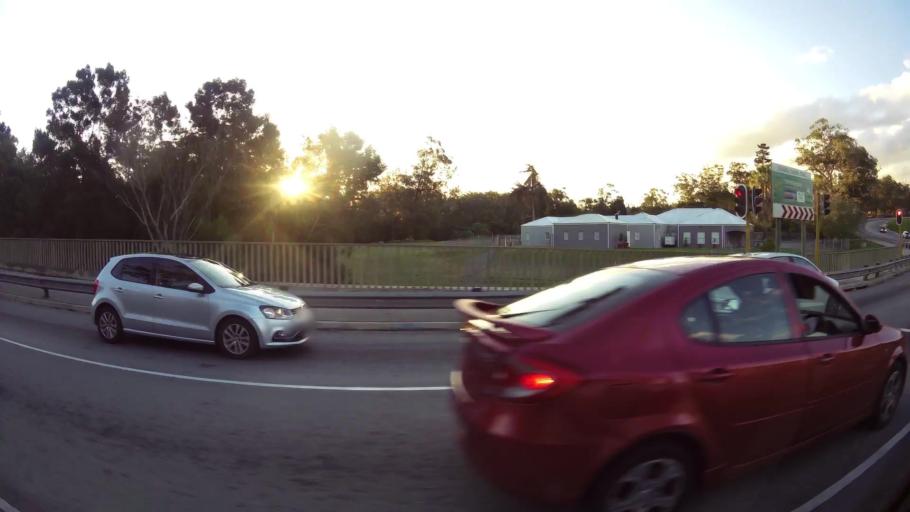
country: ZA
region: Eastern Cape
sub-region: Nelson Mandela Bay Metropolitan Municipality
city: Port Elizabeth
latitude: -33.9589
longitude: 25.5145
